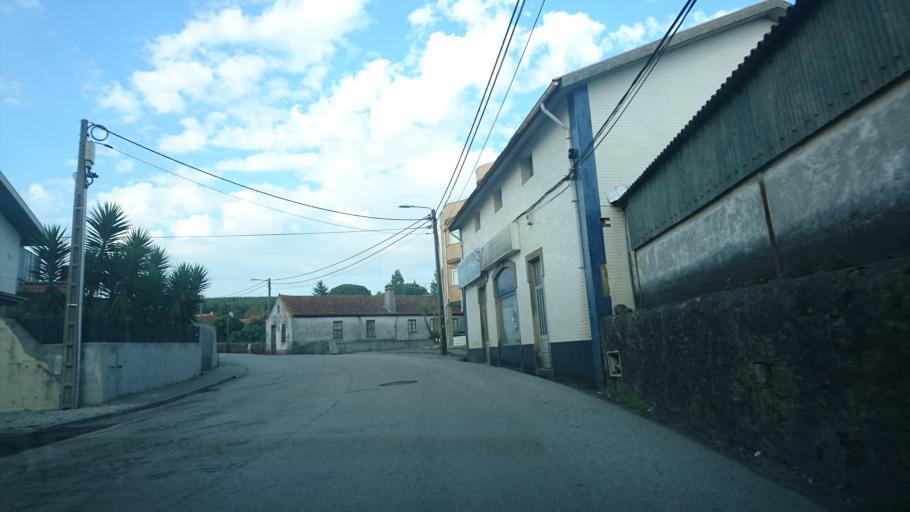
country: PT
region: Aveiro
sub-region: Santa Maria da Feira
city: Sao Joao de Ver
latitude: 40.9543
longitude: -8.5519
